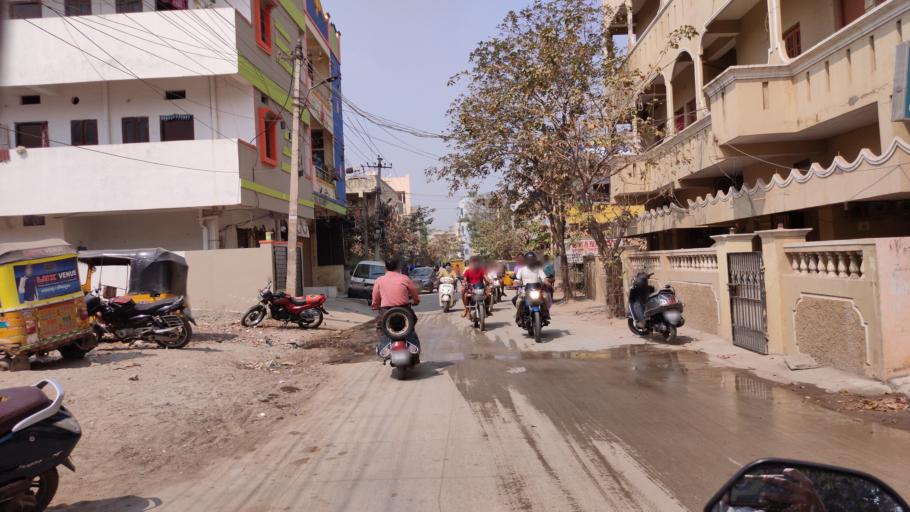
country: IN
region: Telangana
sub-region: Rangareddi
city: Quthbullapur
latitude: 17.4940
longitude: 78.4601
